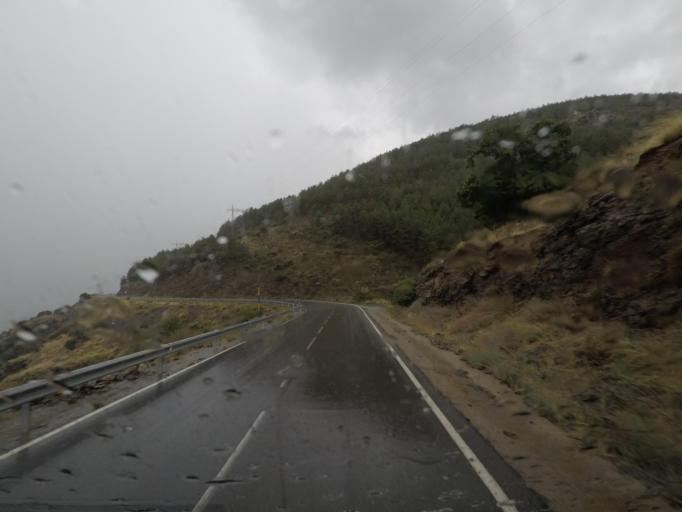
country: ES
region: Andalusia
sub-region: Provincia de Almeria
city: Bayarcal
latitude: 37.0662
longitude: -3.0172
